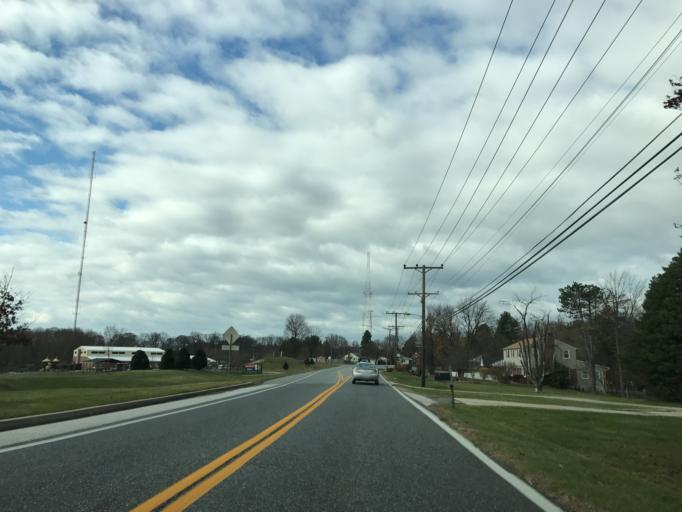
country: US
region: Maryland
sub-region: Baltimore County
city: Hunt Valley
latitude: 39.5134
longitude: -76.5522
